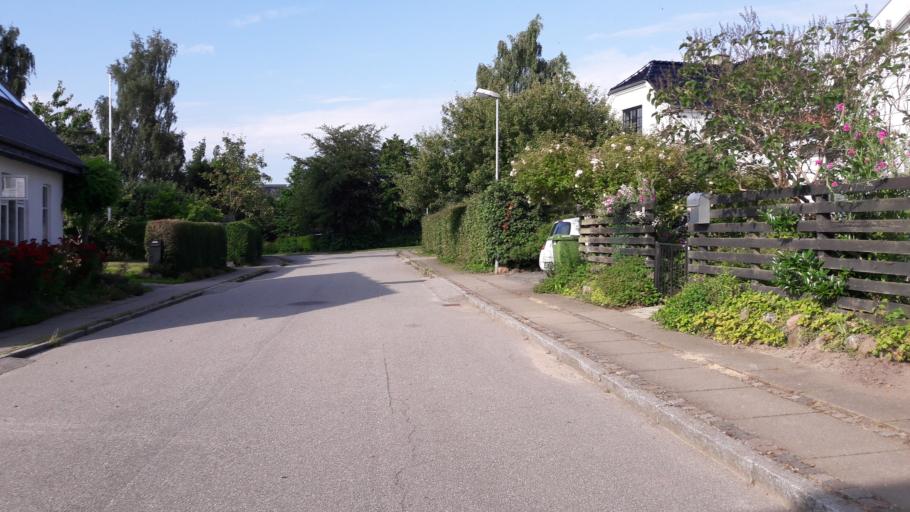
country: DK
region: Central Jutland
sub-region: Arhus Kommune
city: Arhus
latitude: 56.1971
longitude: 10.2176
